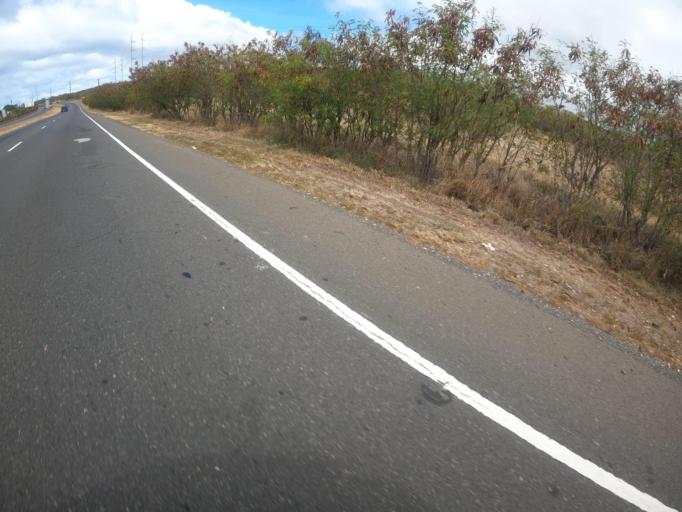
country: US
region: Hawaii
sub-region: Honolulu County
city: Makakilo City
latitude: 21.3400
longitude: -158.1019
